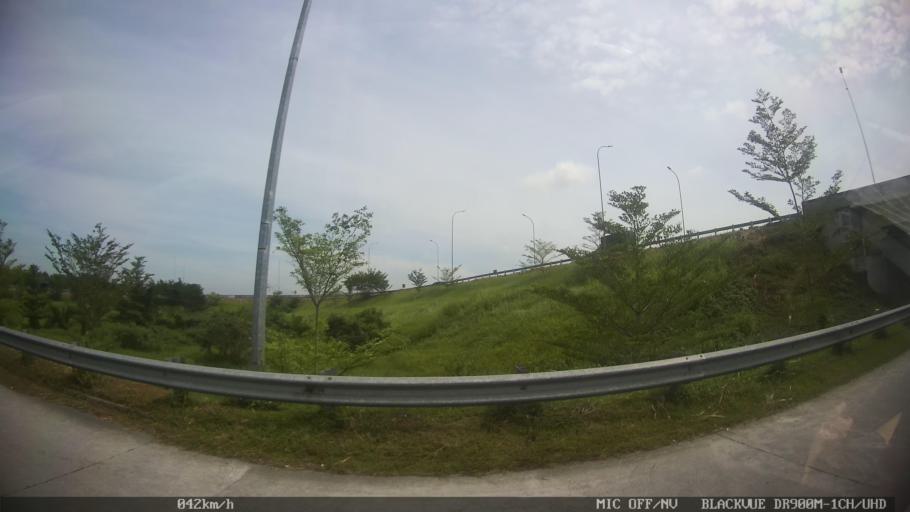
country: ID
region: North Sumatra
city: Medan
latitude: 3.6381
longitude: 98.6355
